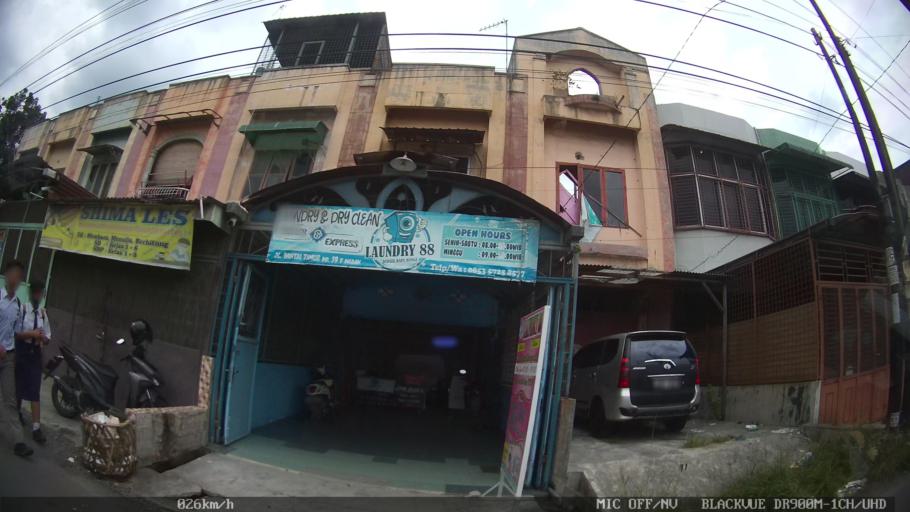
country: ID
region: North Sumatra
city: Sunggal
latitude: 3.6001
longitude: 98.6175
